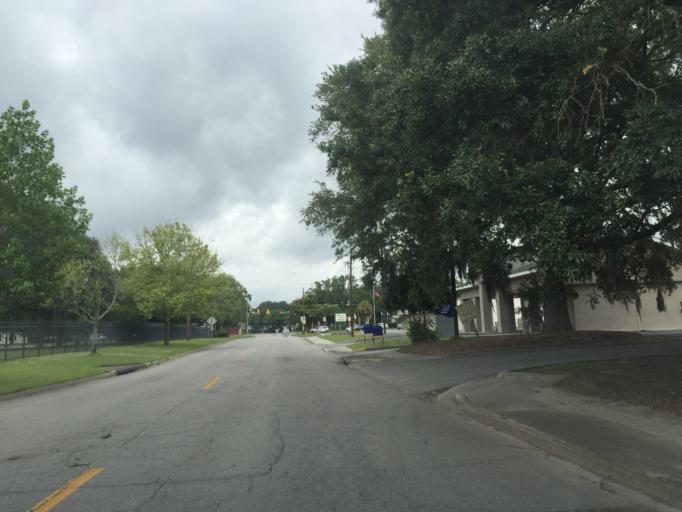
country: US
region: Georgia
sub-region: Chatham County
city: Thunderbolt
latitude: 32.0323
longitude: -81.0937
